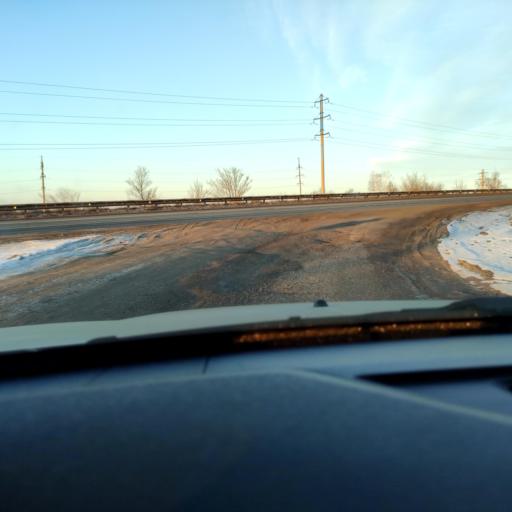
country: RU
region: Samara
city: Smyshlyayevka
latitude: 53.2429
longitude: 50.4792
